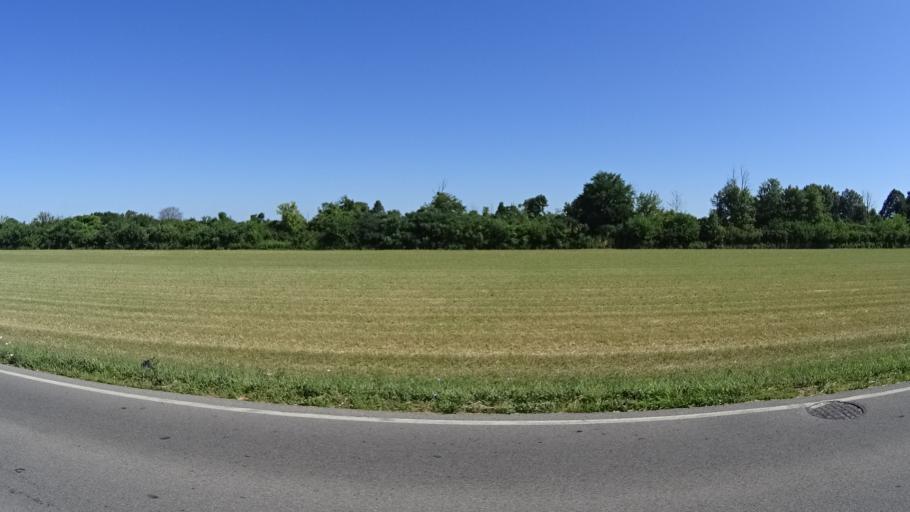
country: US
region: Ohio
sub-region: Erie County
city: Sandusky
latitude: 41.4092
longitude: -82.7201
